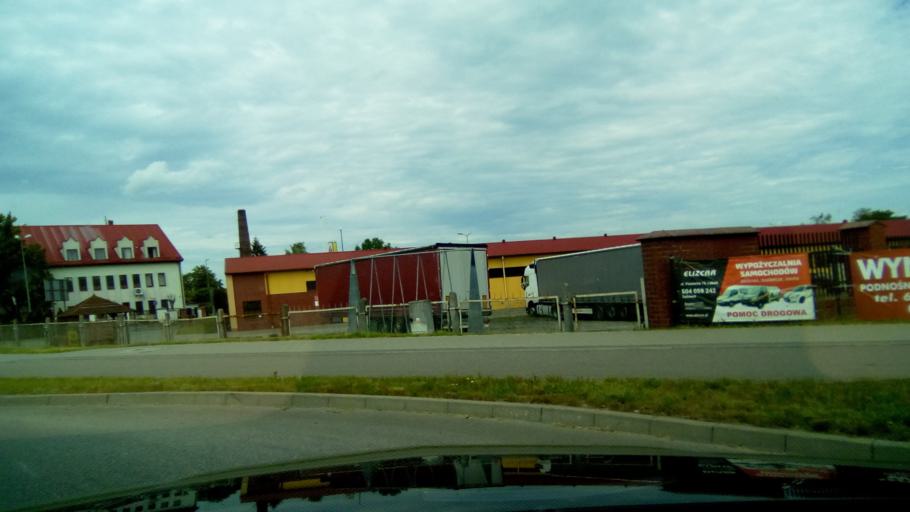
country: PL
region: Pomeranian Voivodeship
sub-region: Powiat leborski
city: Lebork
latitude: 54.5297
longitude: 17.7636
